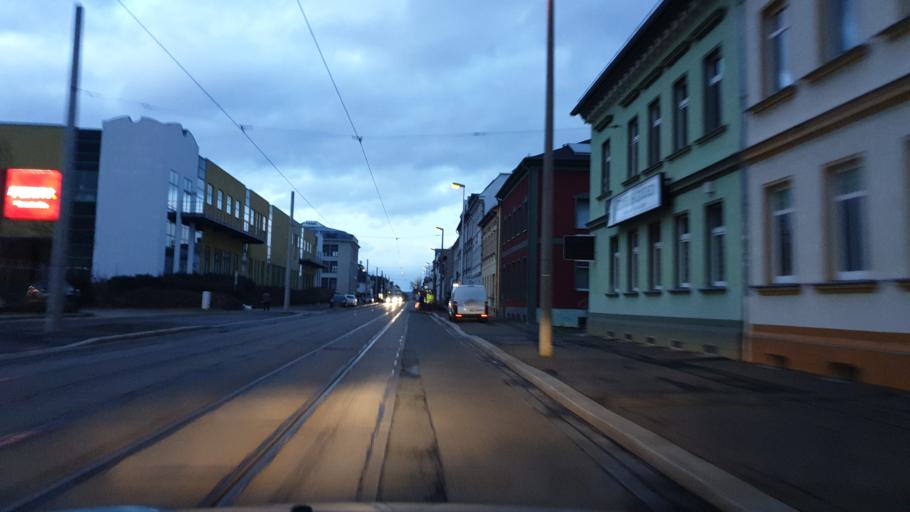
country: DE
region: Thuringia
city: Gera
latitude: 50.8528
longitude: 12.0728
